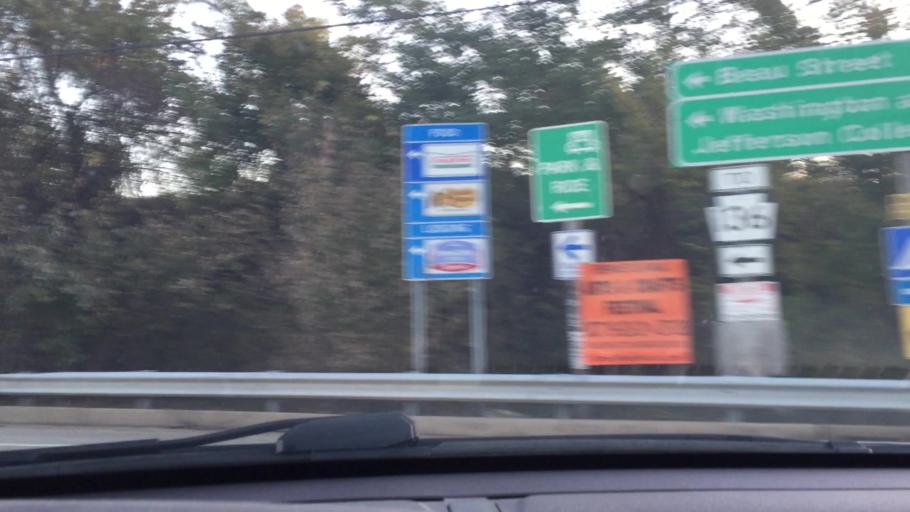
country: US
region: Pennsylvania
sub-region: Washington County
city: East Washington
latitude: 40.1792
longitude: -80.2218
